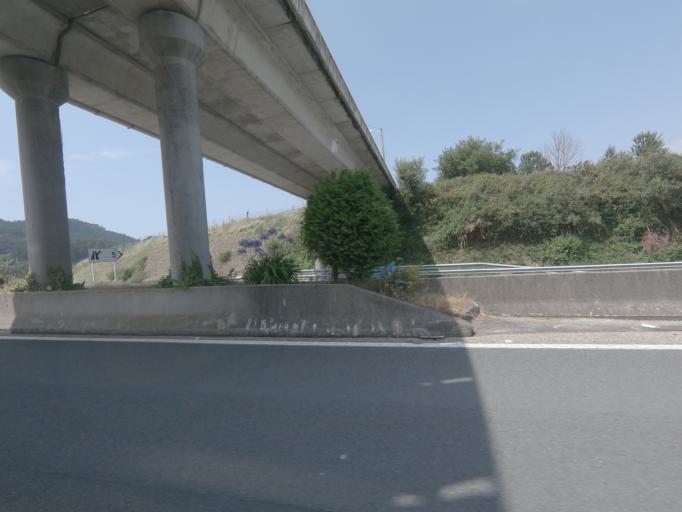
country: ES
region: Galicia
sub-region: Provincia de Pontevedra
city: Baiona
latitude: 42.1003
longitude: -8.8227
